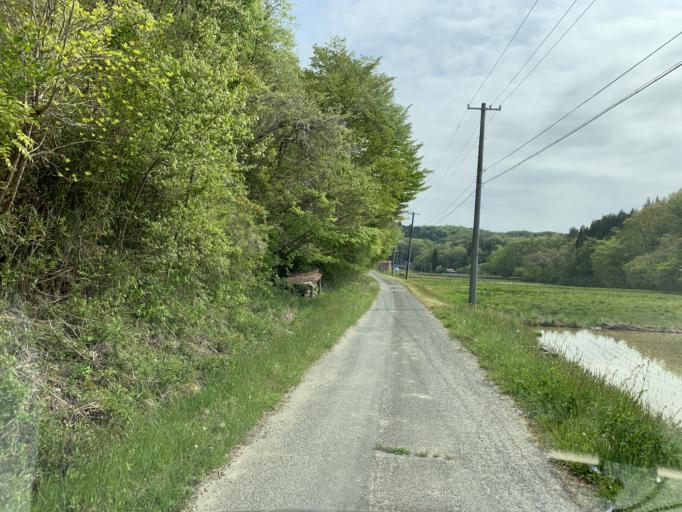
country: JP
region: Iwate
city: Ichinoseki
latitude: 38.8886
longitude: 141.0551
